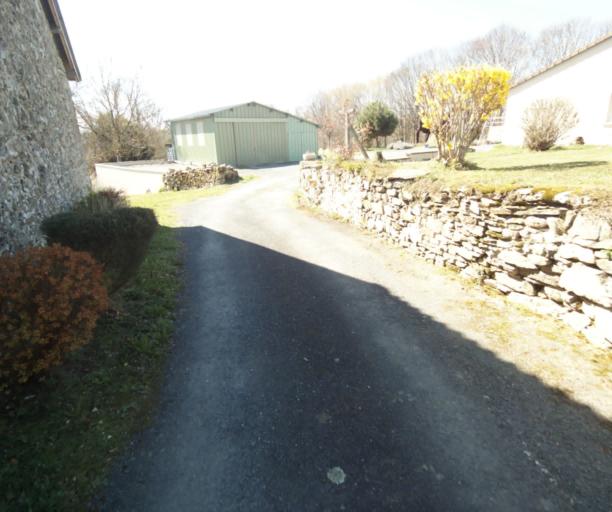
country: FR
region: Limousin
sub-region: Departement de la Correze
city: Saint-Mexant
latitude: 45.2971
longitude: 1.6180
